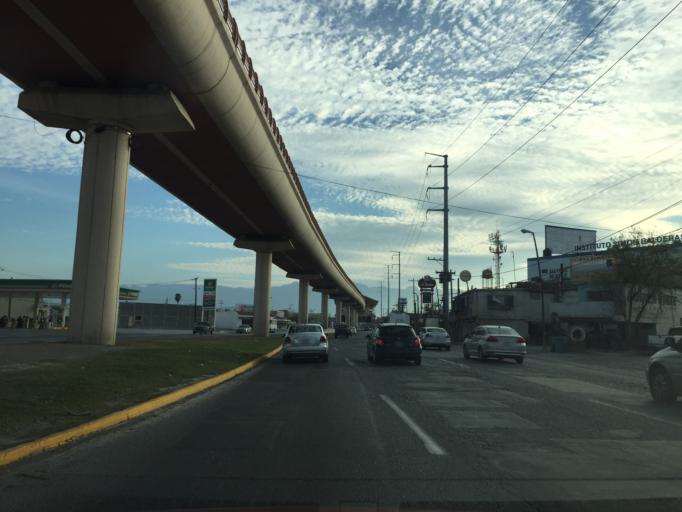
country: MX
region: Nuevo Leon
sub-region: San Nicolas de los Garza
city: San Nicolas de los Garza
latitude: 25.7628
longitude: -100.2944
